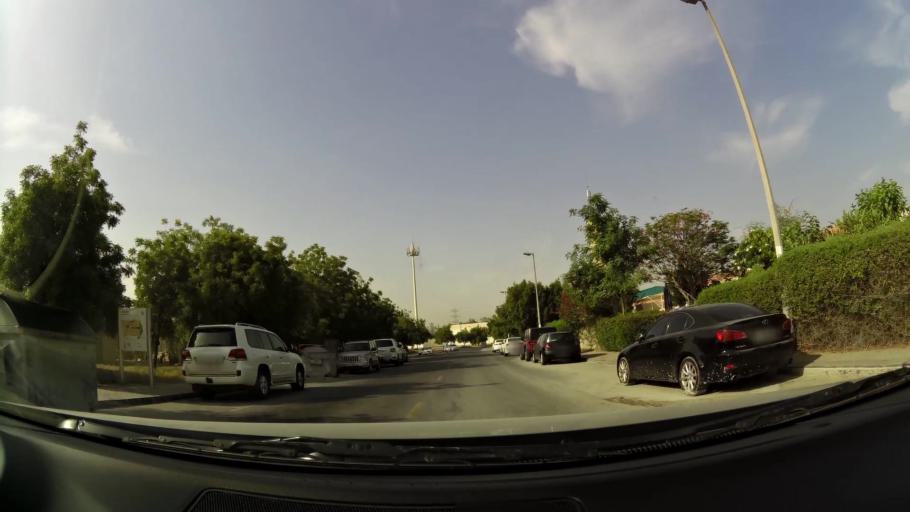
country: AE
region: Ash Shariqah
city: Sharjah
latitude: 25.2236
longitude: 55.3781
